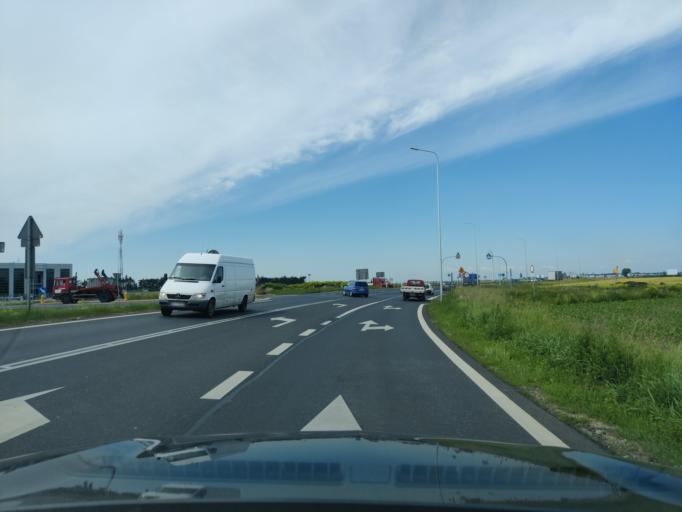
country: PL
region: Greater Poland Voivodeship
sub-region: Powiat grodziski
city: Granowo
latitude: 52.2215
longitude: 16.5825
